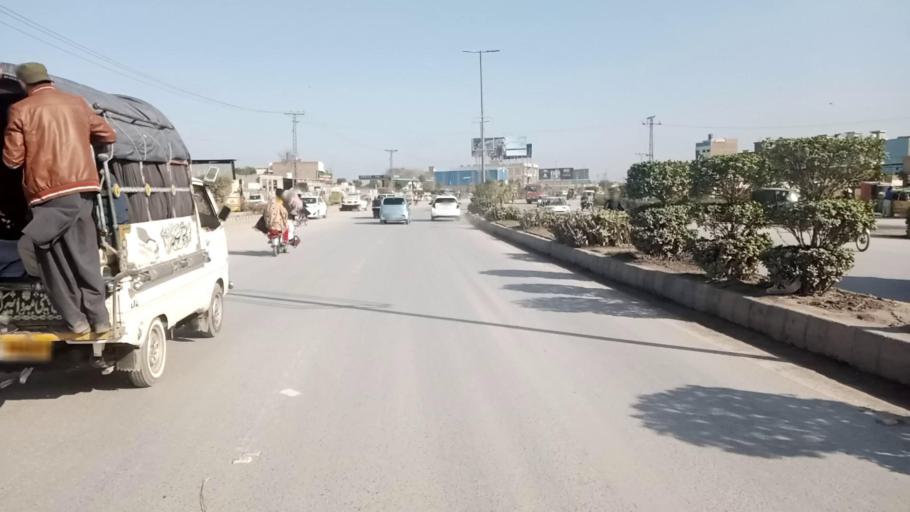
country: PK
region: Khyber Pakhtunkhwa
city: Peshawar
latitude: 34.0336
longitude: 71.6019
